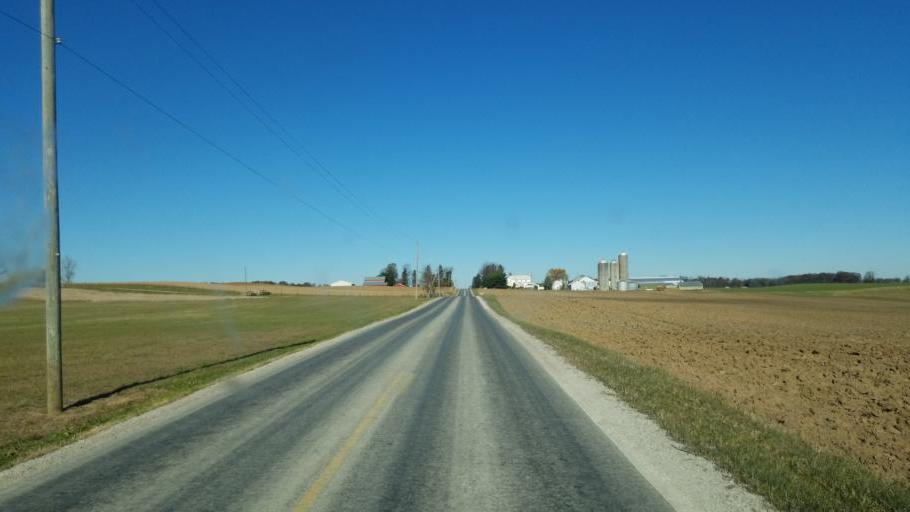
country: US
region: Ohio
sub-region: Huron County
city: Plymouth
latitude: 40.9460
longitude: -82.6194
